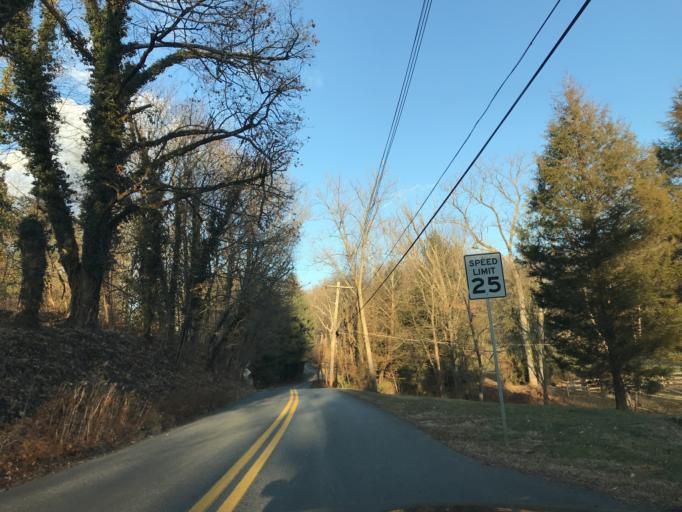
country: US
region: Maryland
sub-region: Baltimore County
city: Lutherville
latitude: 39.3967
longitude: -76.6395
